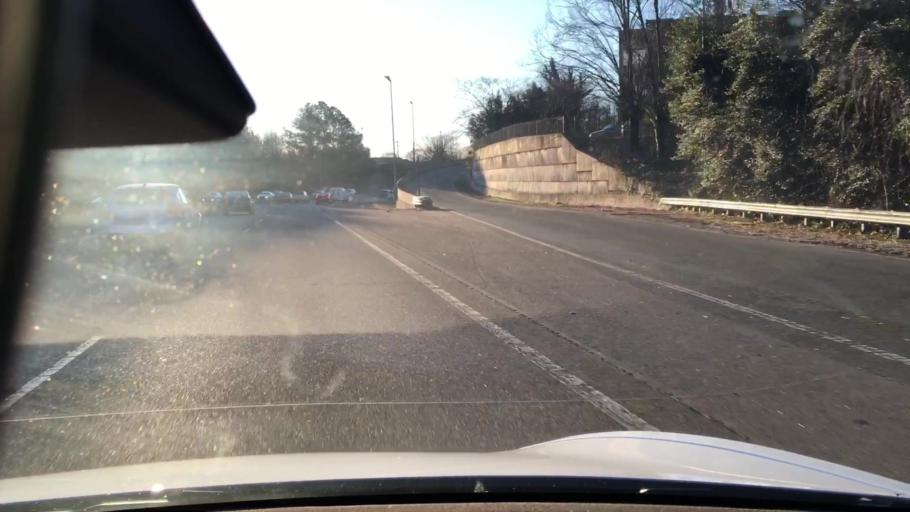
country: US
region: Virginia
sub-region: Chesterfield County
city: Bon Air
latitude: 37.5391
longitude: -77.5308
